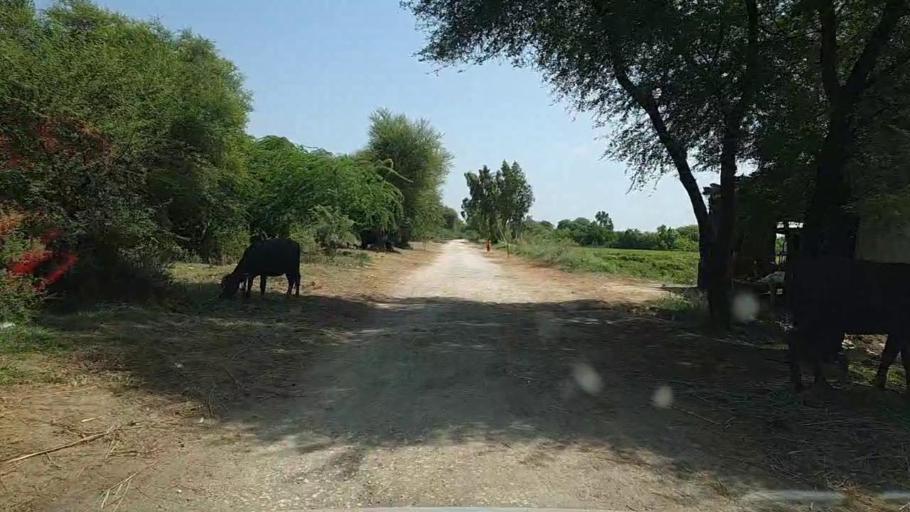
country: PK
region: Sindh
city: Kario
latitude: 24.8483
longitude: 68.6942
